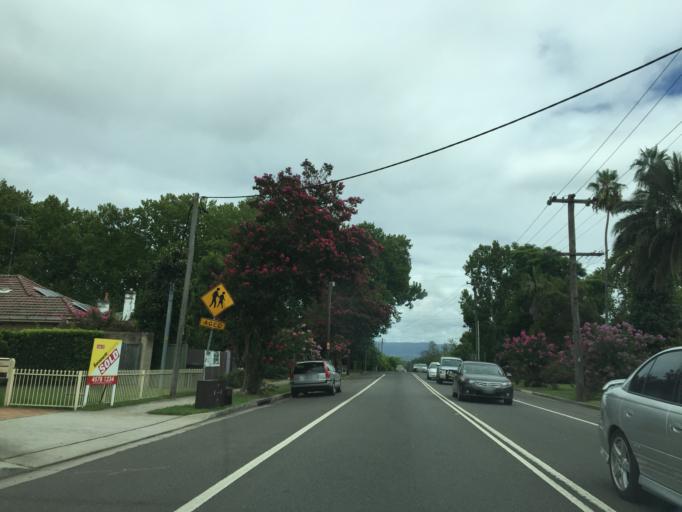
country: AU
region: New South Wales
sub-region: Hawkesbury
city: Richmond
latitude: -33.5961
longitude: 150.7453
